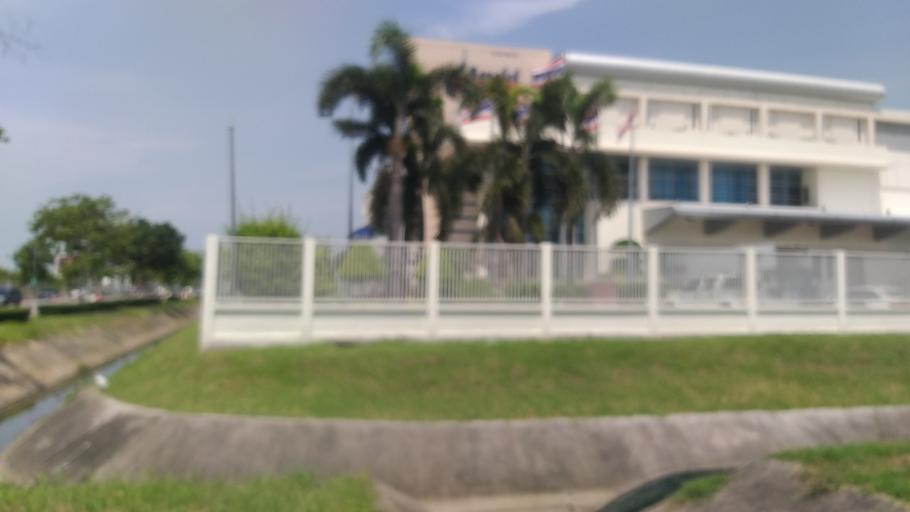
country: TH
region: Bangkok
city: Lat Krabang
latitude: 13.7139
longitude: 100.7647
